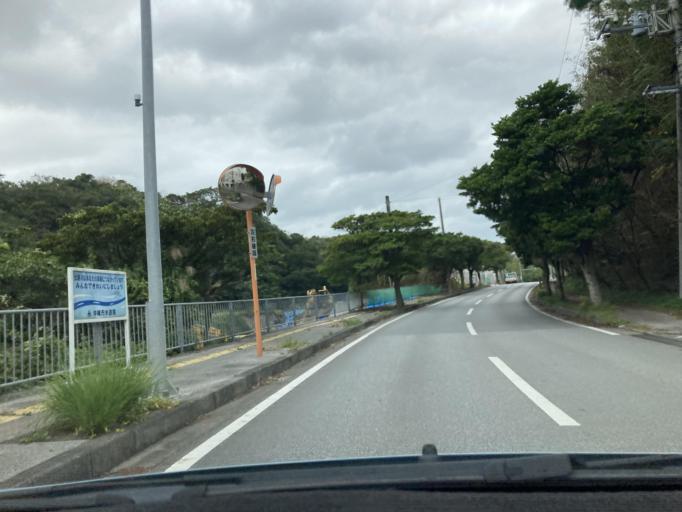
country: JP
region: Okinawa
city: Okinawa
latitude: 26.3452
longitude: 127.8081
